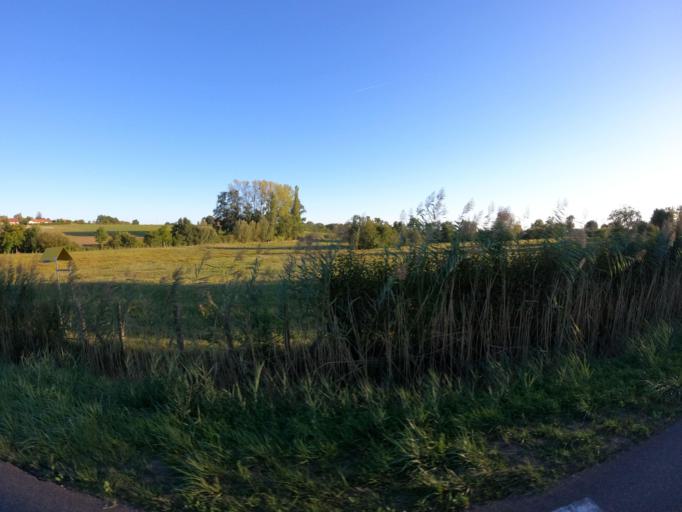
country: FR
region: Bourgogne
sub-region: Departement de Saone-et-Loire
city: Mervans
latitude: 46.7433
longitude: 5.1148
